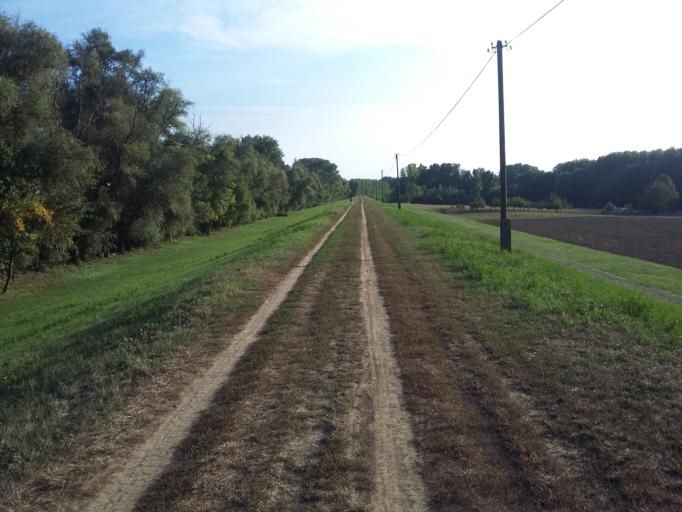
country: HU
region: Csongrad
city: Szeged
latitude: 46.2107
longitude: 20.1189
